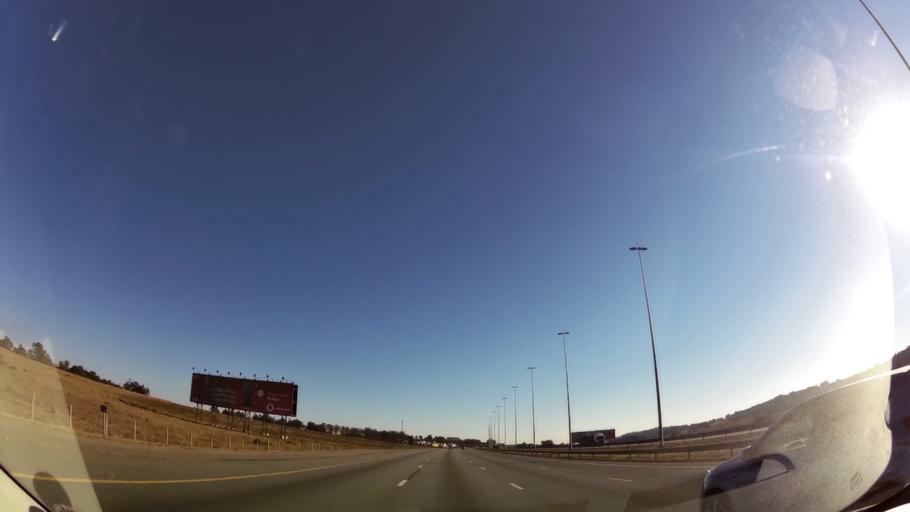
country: ZA
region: Gauteng
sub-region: City of Tshwane Metropolitan Municipality
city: Centurion
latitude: -25.9100
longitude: 28.2572
